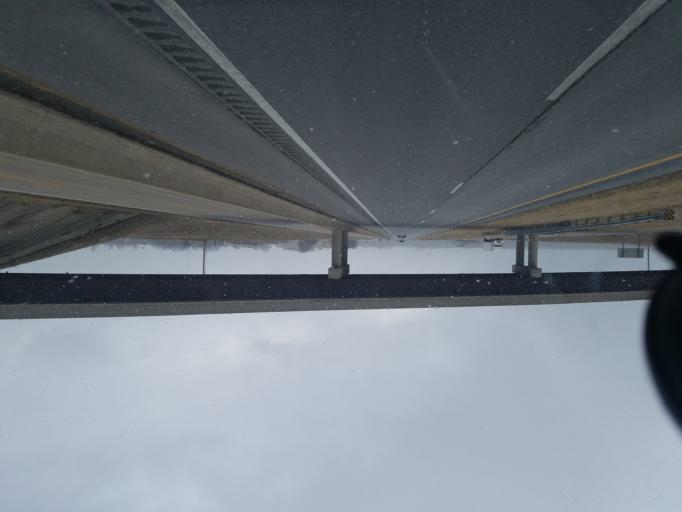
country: US
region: Missouri
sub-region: Randolph County
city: Moberly
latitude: 39.4316
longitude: -92.4161
